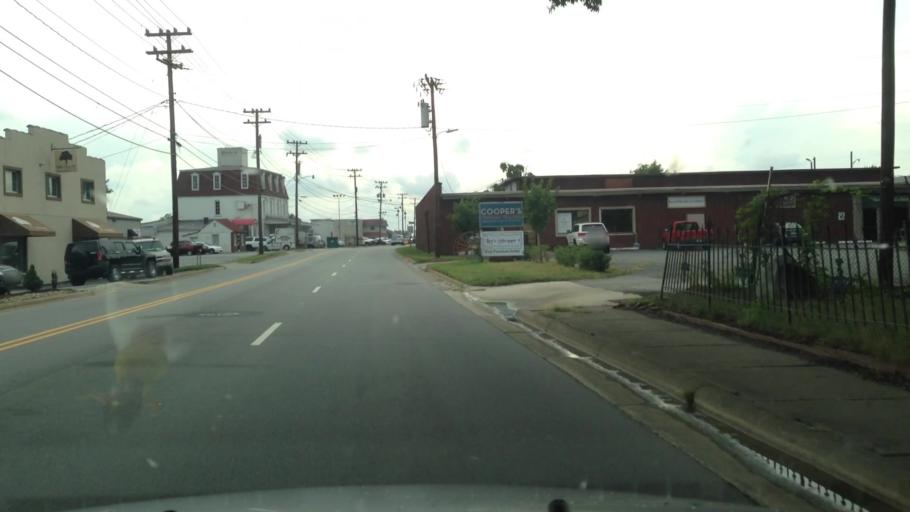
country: US
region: North Carolina
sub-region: Forsyth County
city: Kernersville
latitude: 36.1196
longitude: -80.0683
